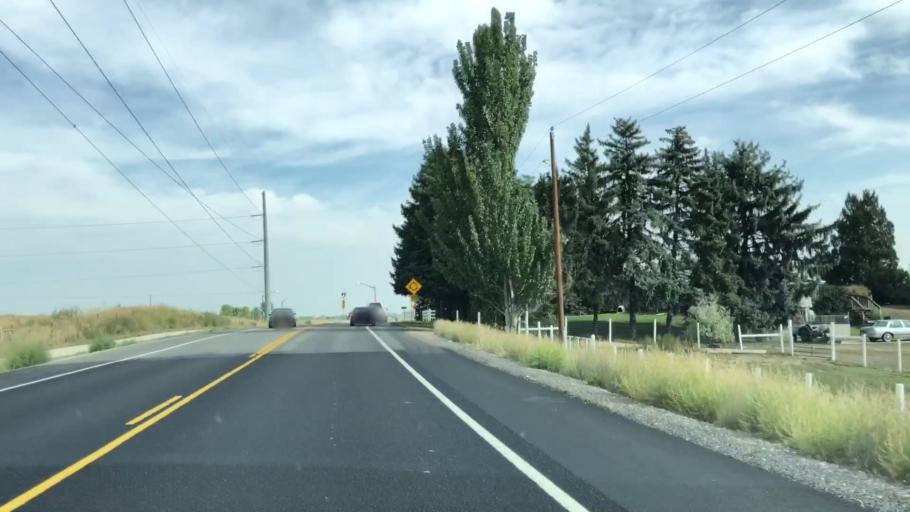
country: US
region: Colorado
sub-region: Larimer County
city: Loveland
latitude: 40.4639
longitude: -105.0441
